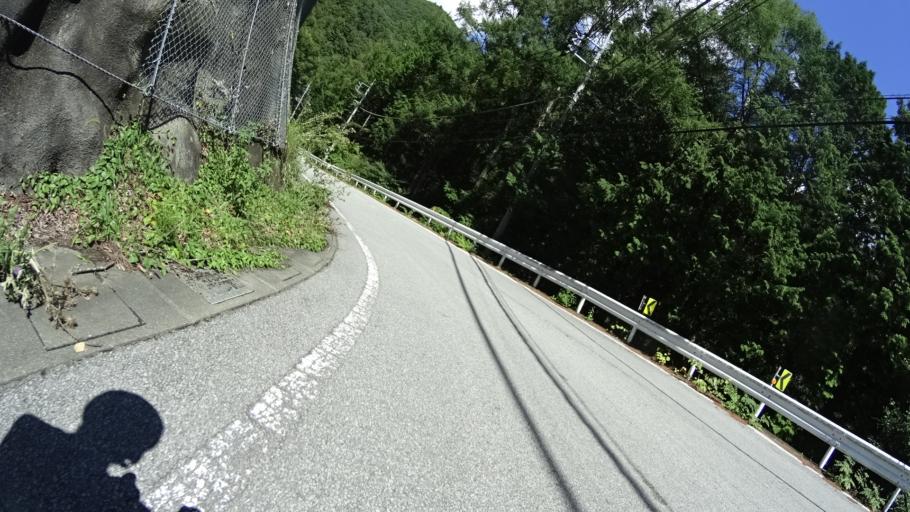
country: JP
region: Yamanashi
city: Enzan
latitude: 35.6581
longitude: 138.8142
